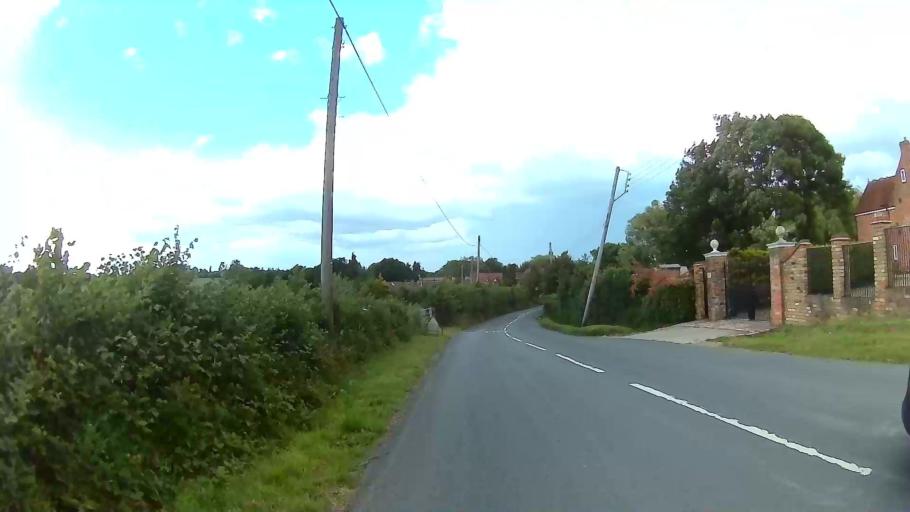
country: GB
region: England
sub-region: Greater London
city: Collier Row
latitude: 51.6284
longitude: 0.1707
